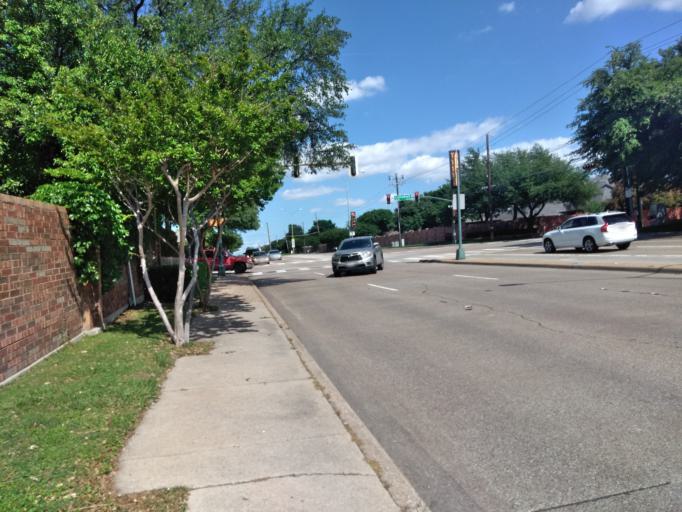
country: US
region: Texas
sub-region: Dallas County
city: Addison
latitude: 32.9983
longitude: -96.8060
